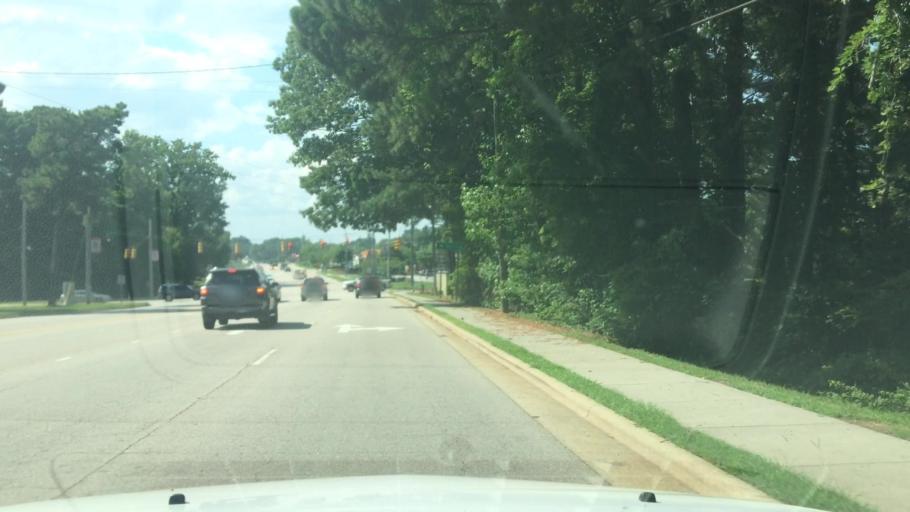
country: US
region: North Carolina
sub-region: Wake County
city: Zebulon
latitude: 35.8354
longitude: -78.3218
